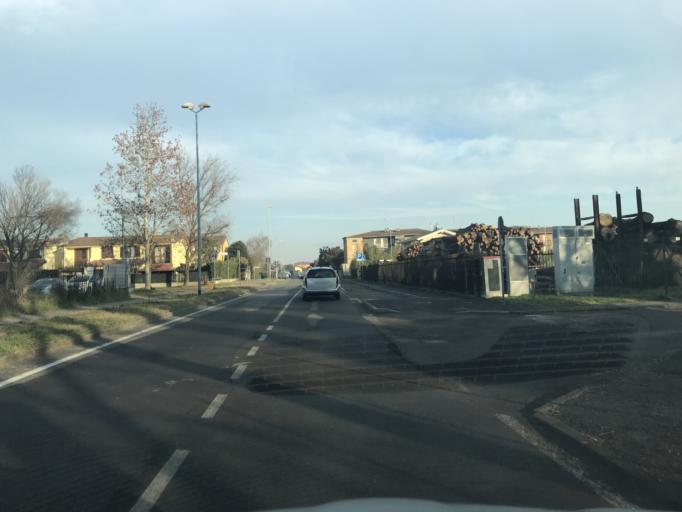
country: IT
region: Lombardy
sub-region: Provincia di Lodi
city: Borgo San Giovanni
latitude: 45.2759
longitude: 9.4264
